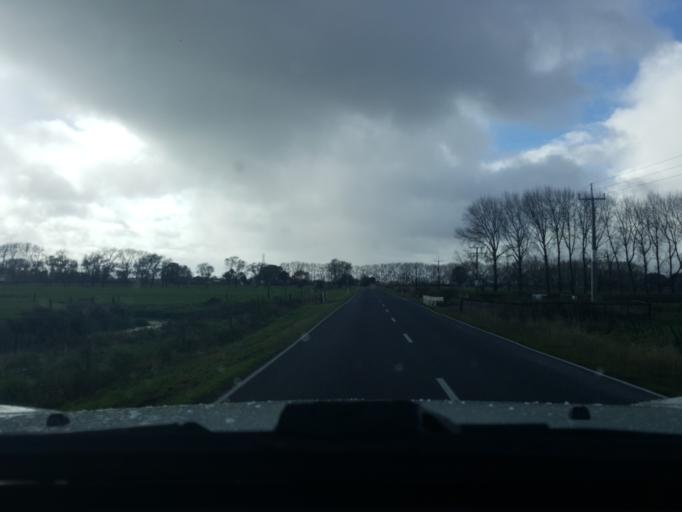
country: NZ
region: Waikato
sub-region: Waikato District
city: Te Kauwhata
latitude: -37.4439
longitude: 175.1211
